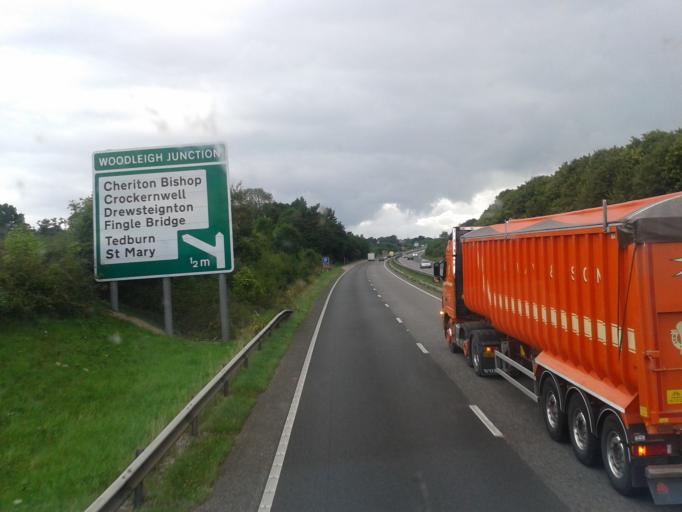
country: GB
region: England
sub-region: Devon
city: Crediton
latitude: 50.7265
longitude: -3.7096
